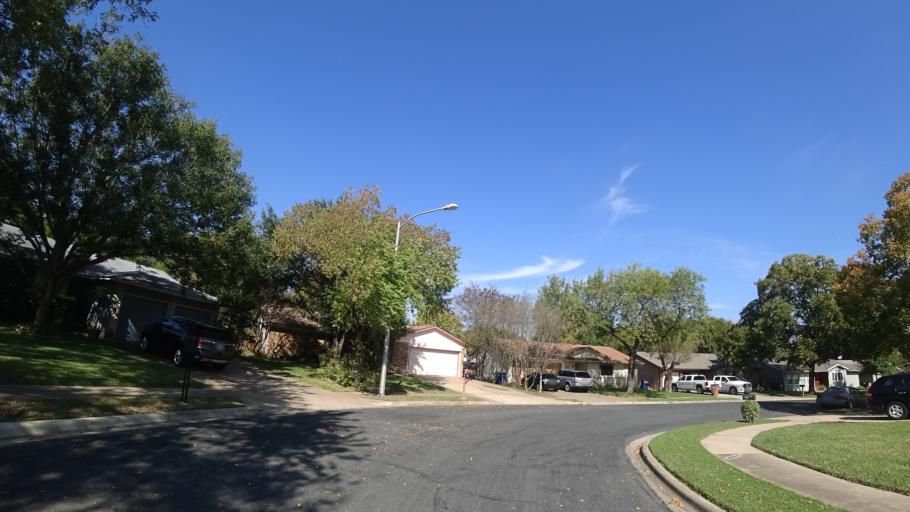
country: US
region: Texas
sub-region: Travis County
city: Shady Hollow
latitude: 30.2125
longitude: -97.8171
